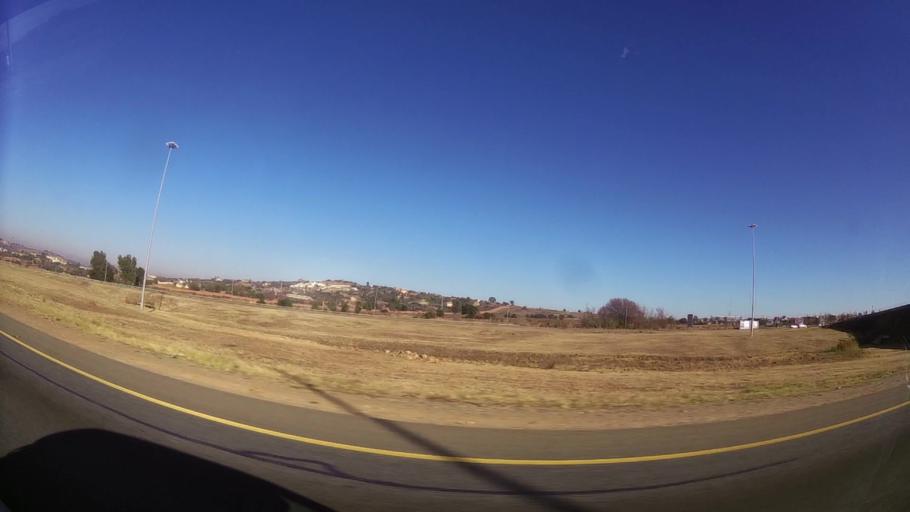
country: ZA
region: Gauteng
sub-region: City of Tshwane Metropolitan Municipality
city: Centurion
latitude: -25.8659
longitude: 28.2536
